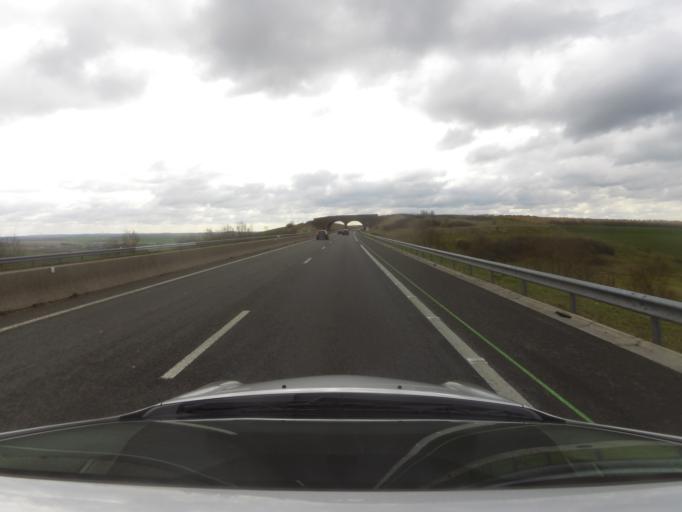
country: FR
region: Nord-Pas-de-Calais
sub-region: Departement du Pas-de-Calais
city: Camiers
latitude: 50.5651
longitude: 1.6590
